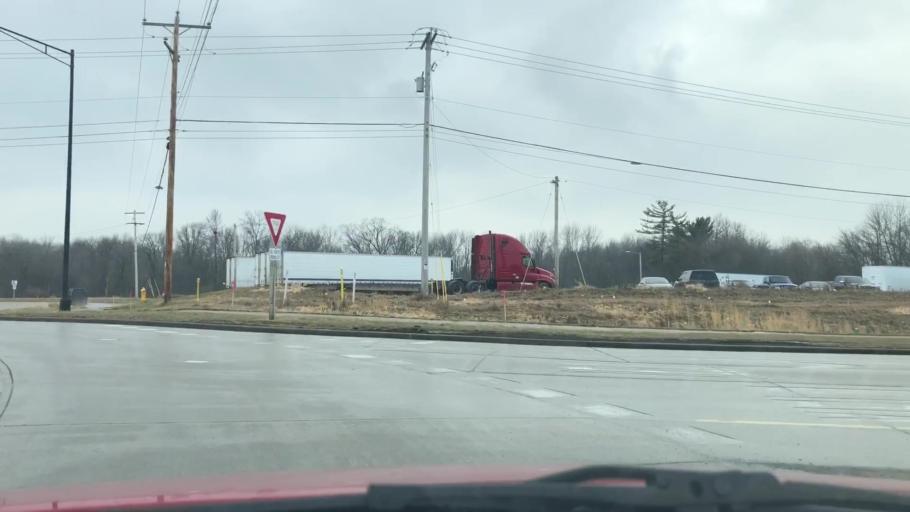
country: US
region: Wisconsin
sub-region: Brown County
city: De Pere
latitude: 44.4537
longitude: -88.0924
